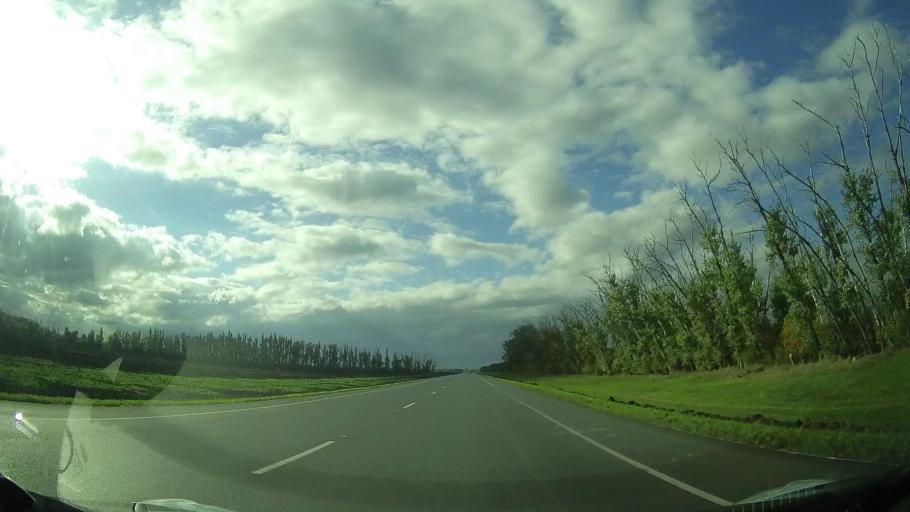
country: RU
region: Rostov
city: Tselina
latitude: 46.5309
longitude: 40.9424
